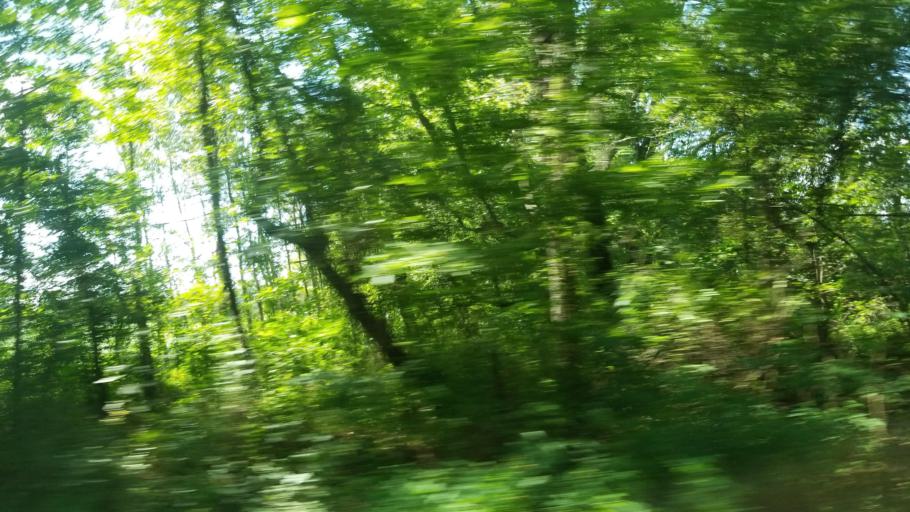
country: US
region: Illinois
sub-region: Williamson County
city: Johnston City
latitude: 37.7698
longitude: -88.8129
